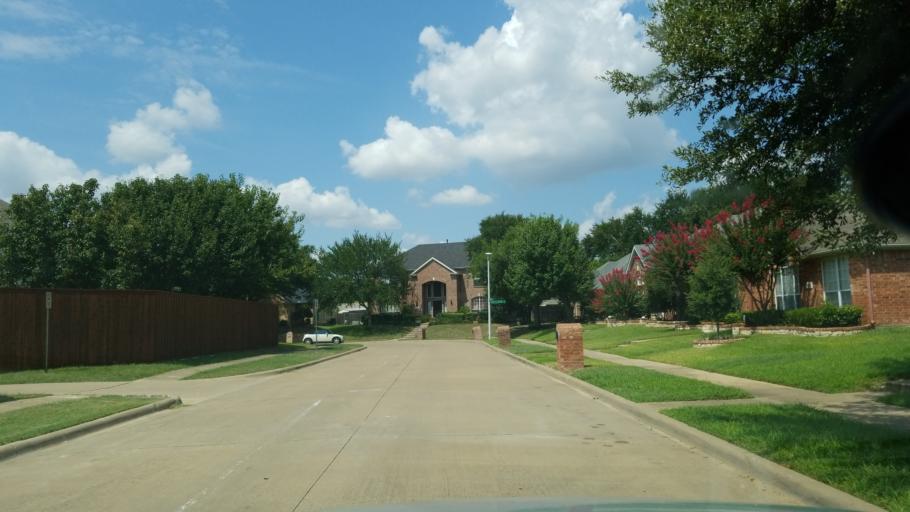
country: US
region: Texas
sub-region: Dallas County
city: Garland
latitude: 32.9228
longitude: -96.6587
